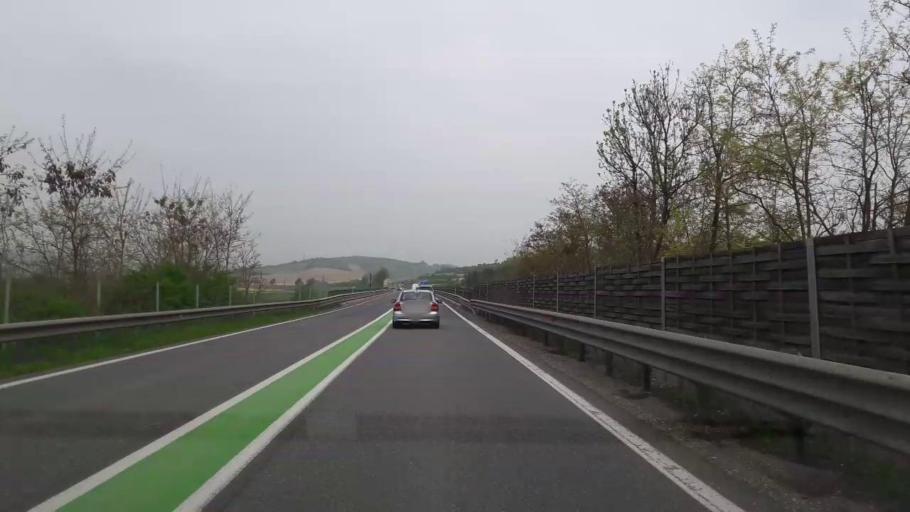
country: AT
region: Lower Austria
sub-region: Politischer Bezirk Hollabrunn
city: Gollersdorf
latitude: 48.5036
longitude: 16.1012
